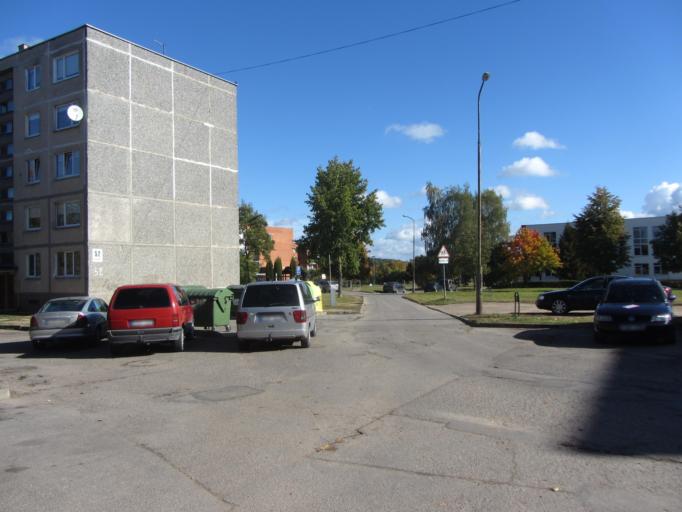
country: LT
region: Utenos apskritis
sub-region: Utena
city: Utena
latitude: 55.5087
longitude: 25.6020
